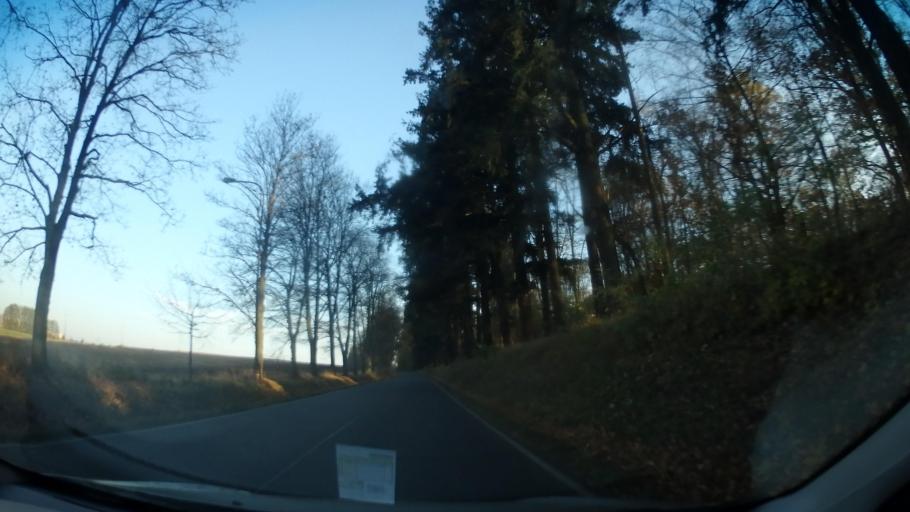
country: CZ
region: Central Bohemia
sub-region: Okres Benesov
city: Benesov
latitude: 49.7815
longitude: 14.6663
